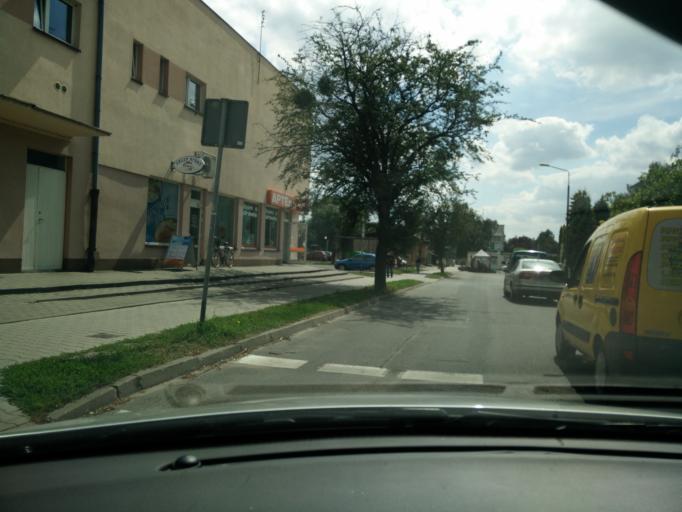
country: PL
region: Greater Poland Voivodeship
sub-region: Powiat sredzki
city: Sroda Wielkopolska
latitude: 52.2262
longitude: 17.2727
